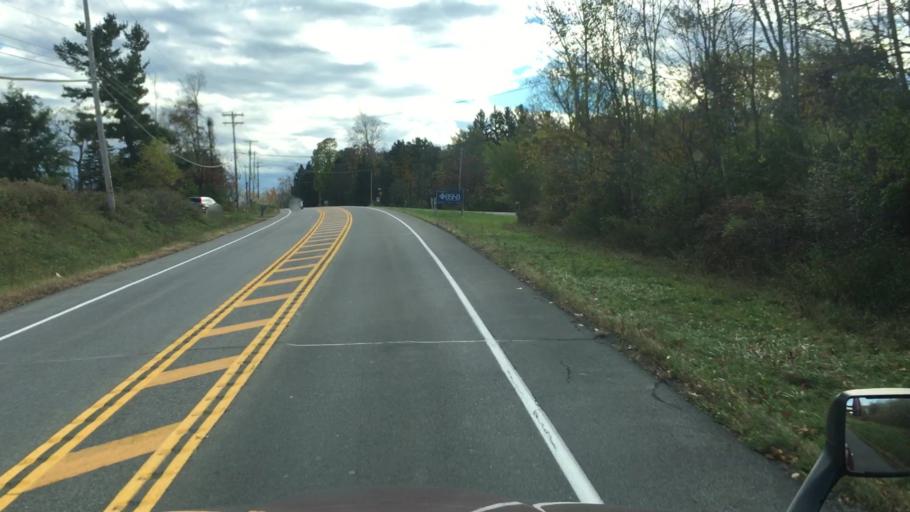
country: US
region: New York
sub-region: Saratoga County
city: Ballston Spa
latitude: 42.9692
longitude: -73.8634
